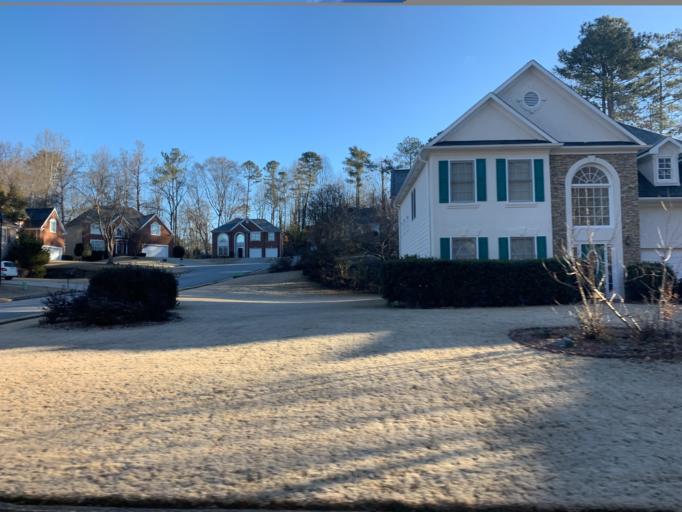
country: US
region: Georgia
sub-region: Gwinnett County
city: Mountain Park
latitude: 33.8665
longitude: -84.1109
